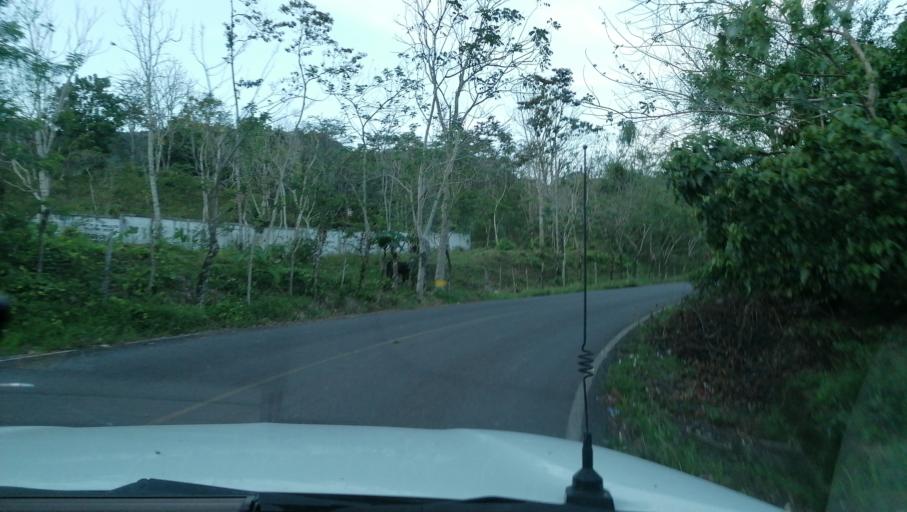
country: MX
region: Chiapas
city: Ostuacan
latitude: 17.4213
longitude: -93.3390
